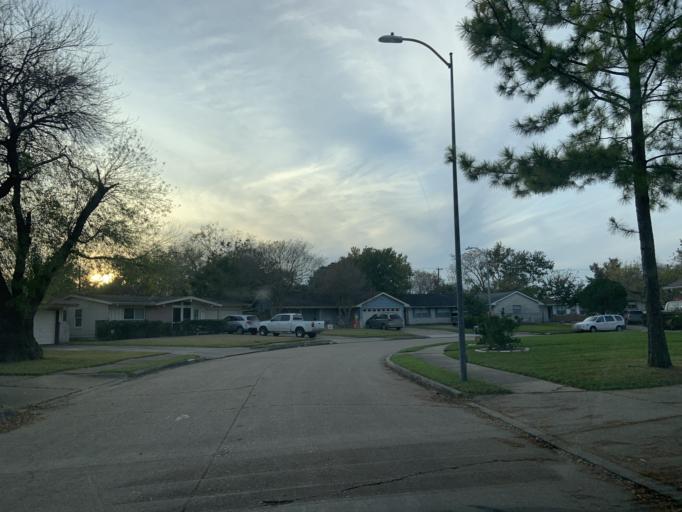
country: US
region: Texas
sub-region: Harris County
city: Bellaire
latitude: 29.6931
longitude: -95.5089
